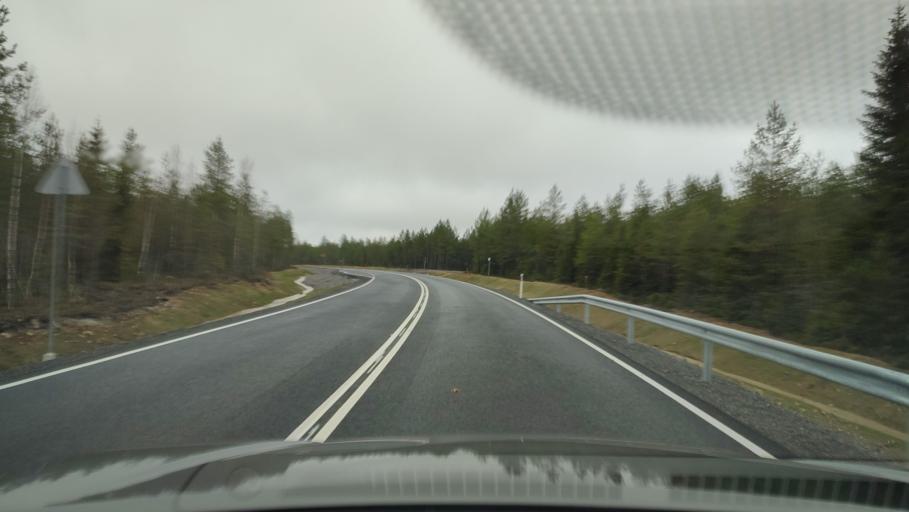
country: FI
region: Southern Ostrobothnia
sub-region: Suupohja
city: Kauhajoki
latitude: 62.2931
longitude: 22.0535
